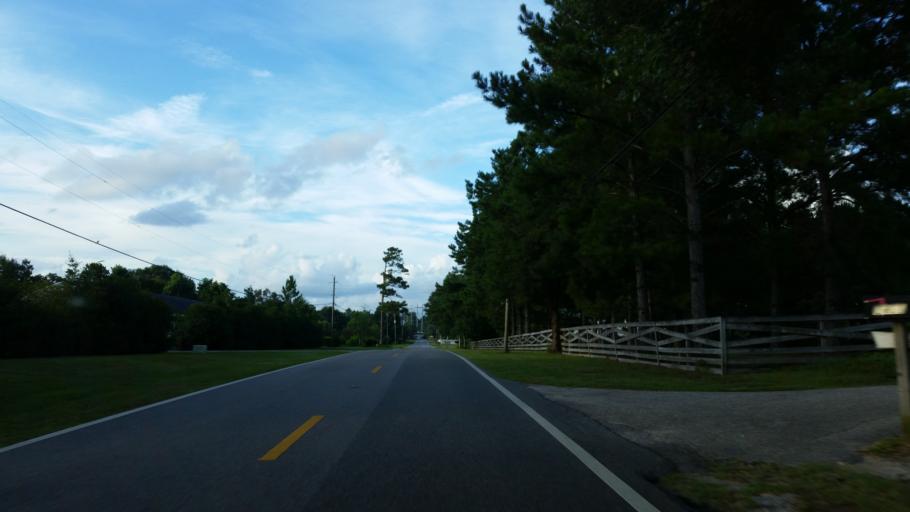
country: US
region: Florida
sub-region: Escambia County
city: Bellview
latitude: 30.5006
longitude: -87.3313
